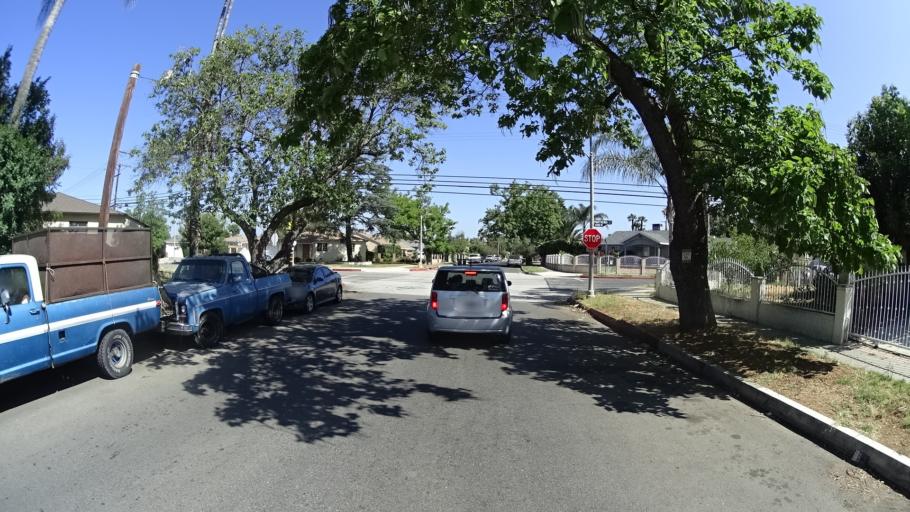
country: US
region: California
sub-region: Los Angeles County
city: Van Nuys
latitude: 34.2288
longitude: -118.4470
